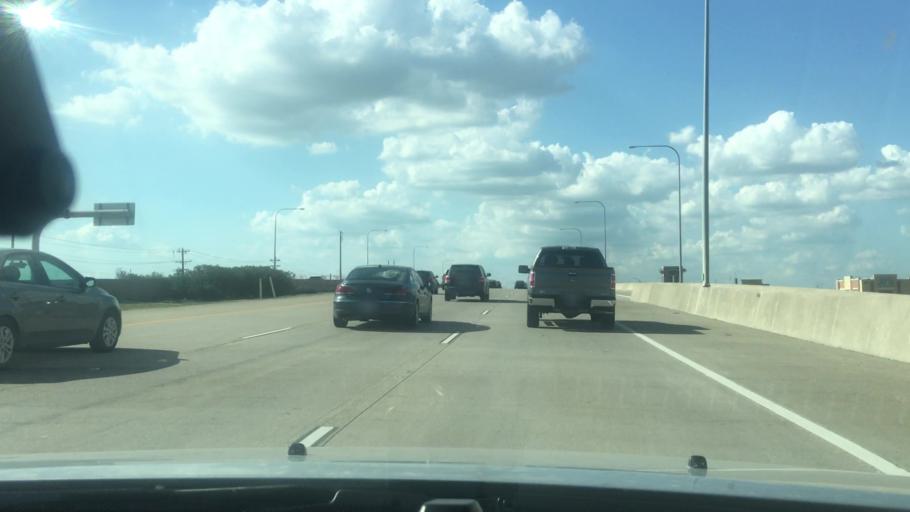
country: US
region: Texas
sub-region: Collin County
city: Frisco
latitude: 33.1505
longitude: -96.8397
